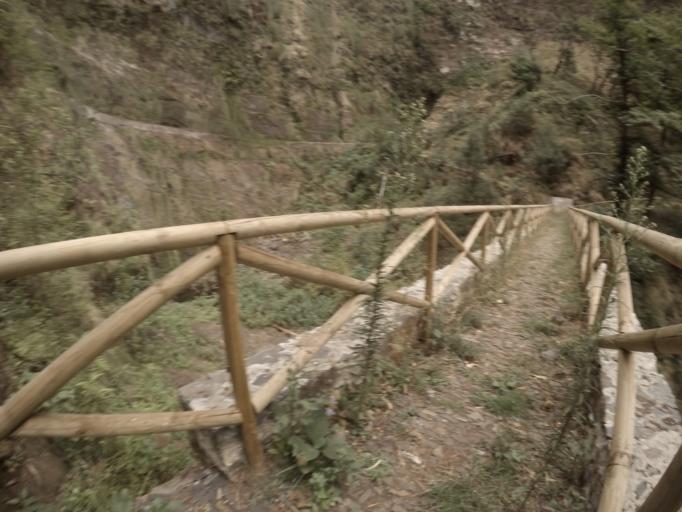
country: PT
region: Madeira
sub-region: Funchal
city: Nossa Senhora do Monte
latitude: 32.6889
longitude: -16.9106
